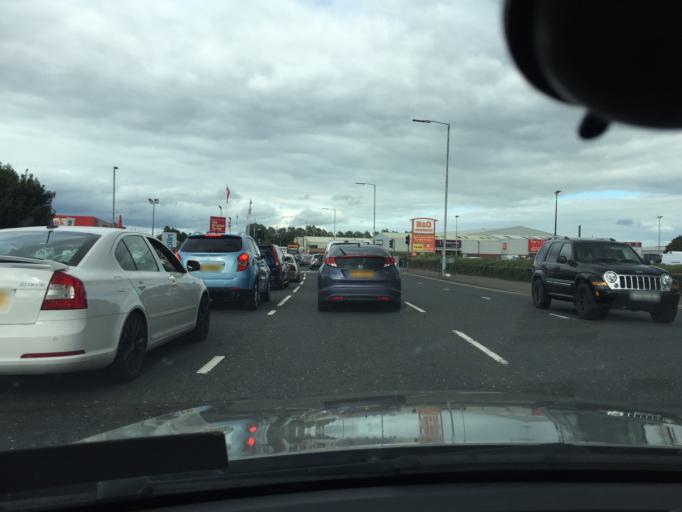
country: GB
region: Northern Ireland
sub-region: City of Belfast
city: Belfast
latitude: 54.5763
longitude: -5.9642
